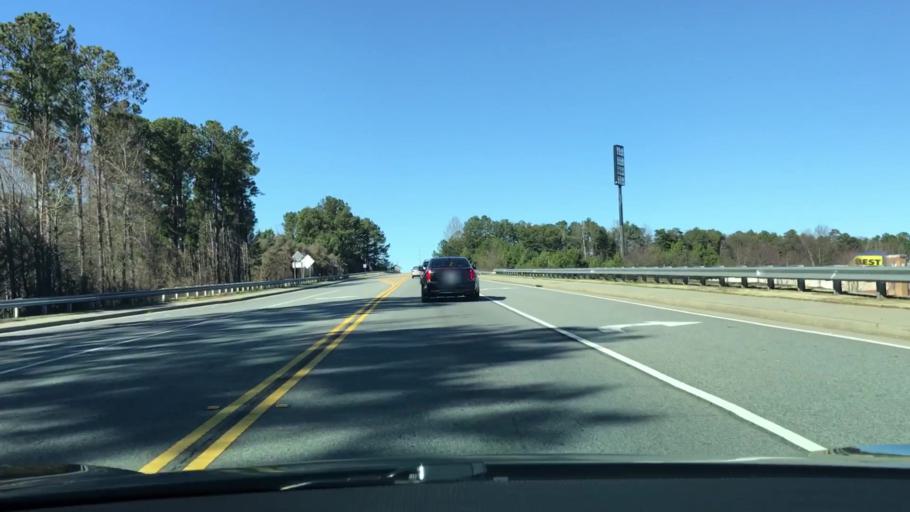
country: US
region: Georgia
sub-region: Forsyth County
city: Cumming
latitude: 34.1910
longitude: -84.1304
